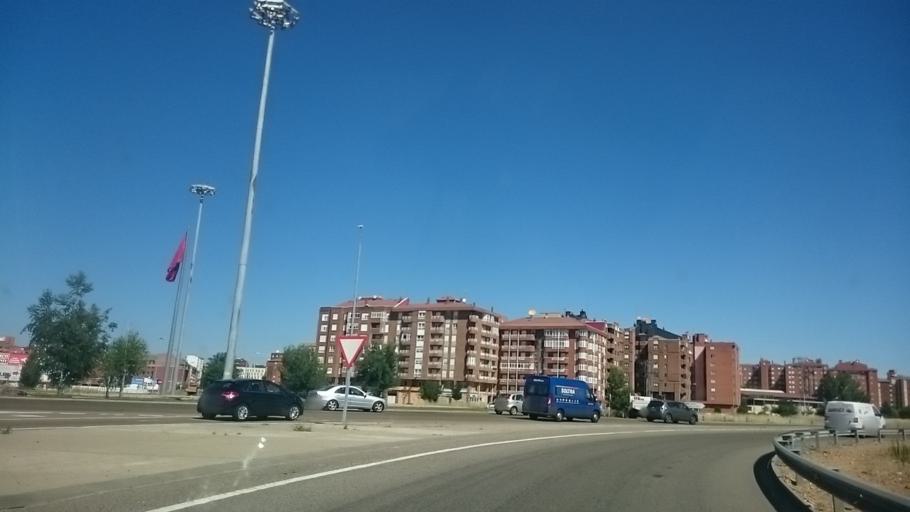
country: ES
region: Castille and Leon
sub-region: Provincia de Leon
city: Leon
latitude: 42.5877
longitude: -5.5554
